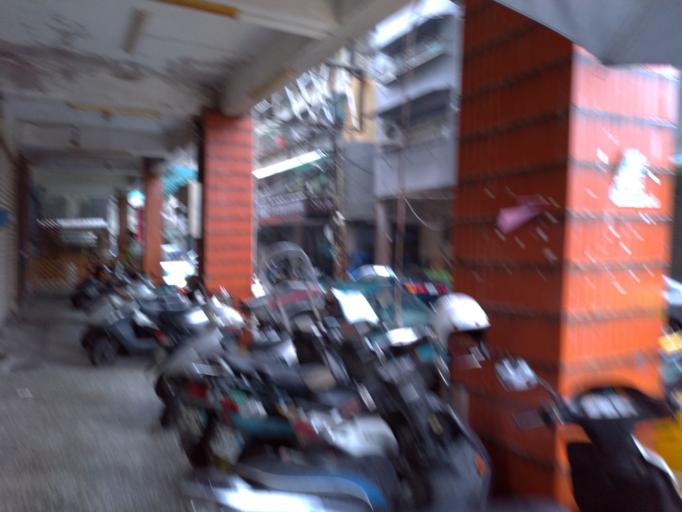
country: TW
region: Taiwan
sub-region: Keelung
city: Keelung
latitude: 25.0824
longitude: 121.6979
